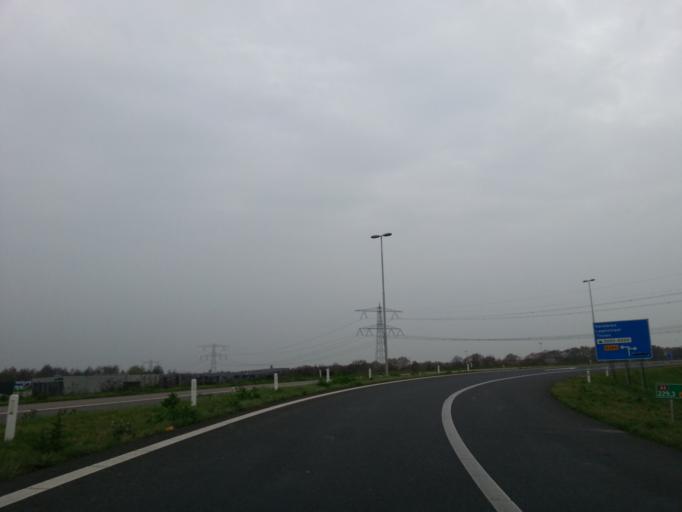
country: NL
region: North Brabant
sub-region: Gemeente Bergen op Zoom
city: Lepelstraat
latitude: 51.5419
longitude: 4.2920
